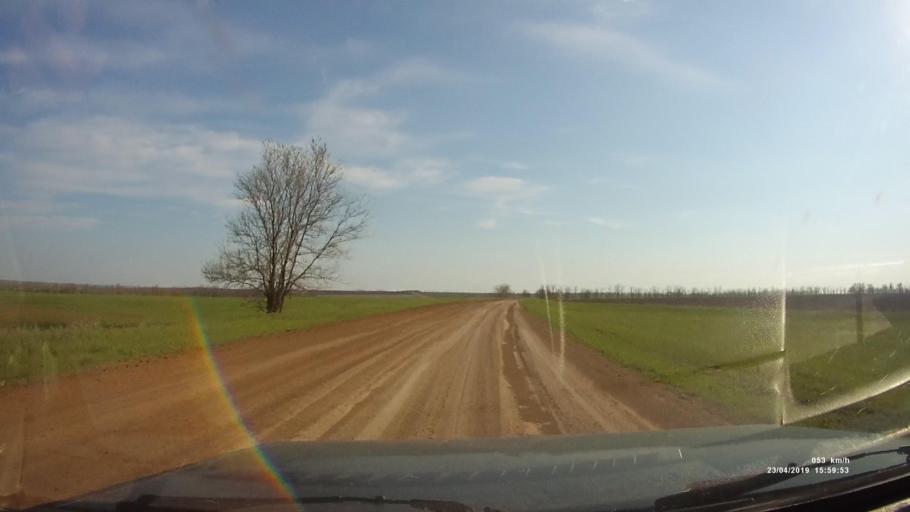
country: RU
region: Rostov
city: Remontnoye
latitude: 46.5132
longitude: 43.1093
